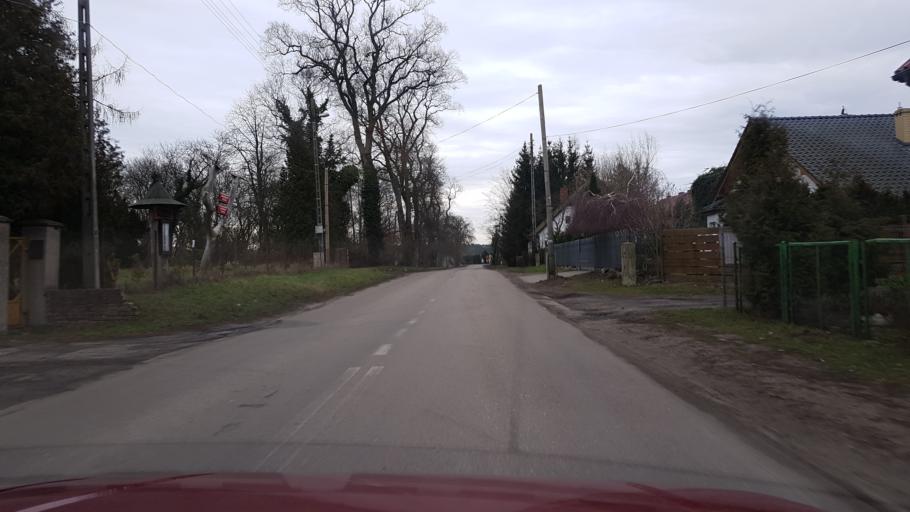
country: PL
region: West Pomeranian Voivodeship
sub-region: Powiat policki
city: Dobra
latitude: 53.5471
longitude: 14.4624
